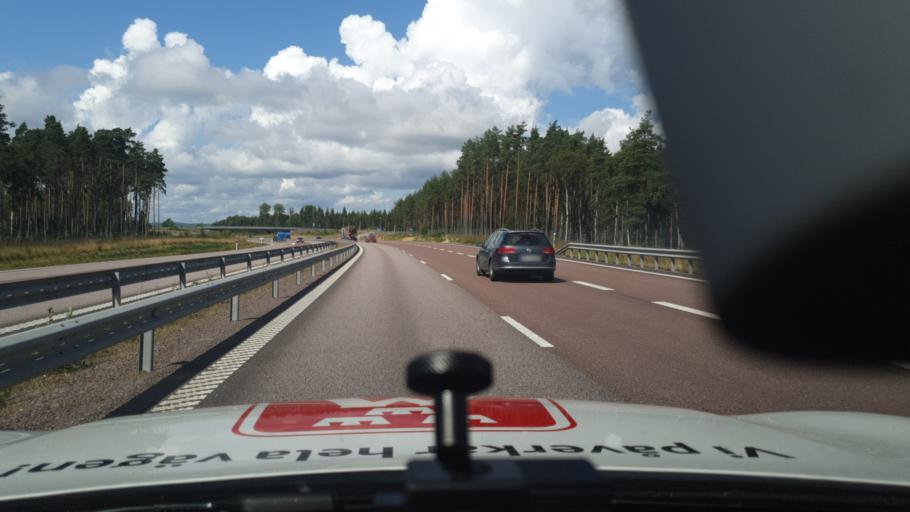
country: SE
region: Vaermland
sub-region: Kils Kommun
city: Kil
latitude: 59.3910
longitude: 13.2916
